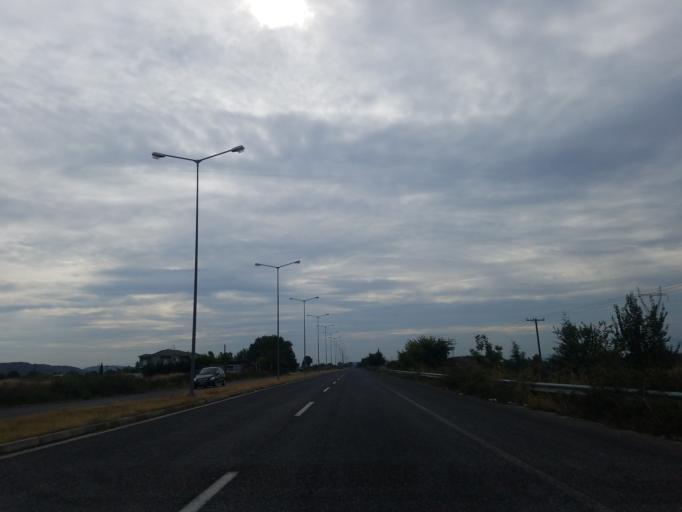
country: GR
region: Thessaly
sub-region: Trikala
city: Vasiliki
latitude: 39.6331
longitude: 21.7009
